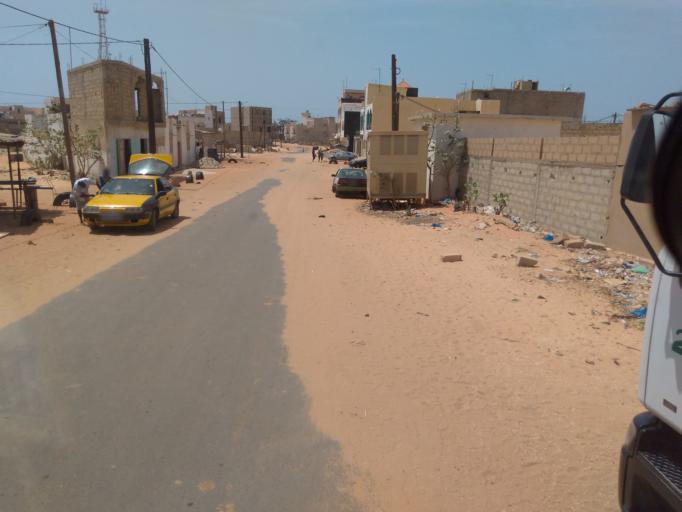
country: SN
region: Dakar
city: Pikine
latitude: 14.7840
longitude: -17.3337
